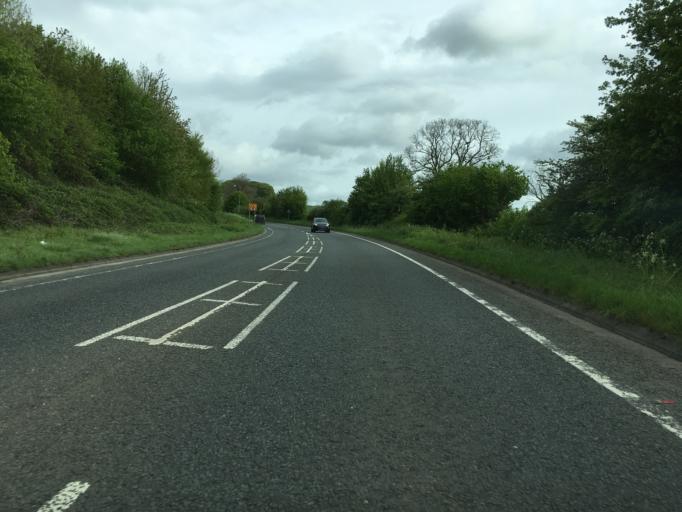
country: GB
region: England
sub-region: Bath and North East Somerset
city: Peasedown Saint John
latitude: 51.3146
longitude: -2.4133
